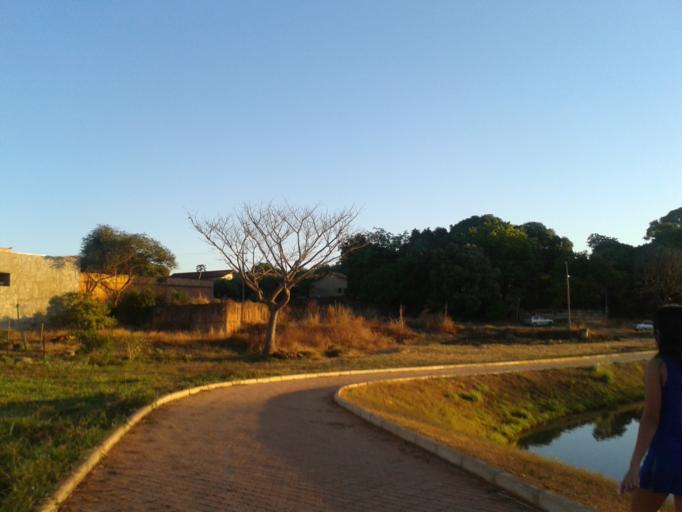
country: BR
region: Goias
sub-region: Sao Miguel Do Araguaia
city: Sao Miguel do Araguaia
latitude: -13.2688
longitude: -50.1639
